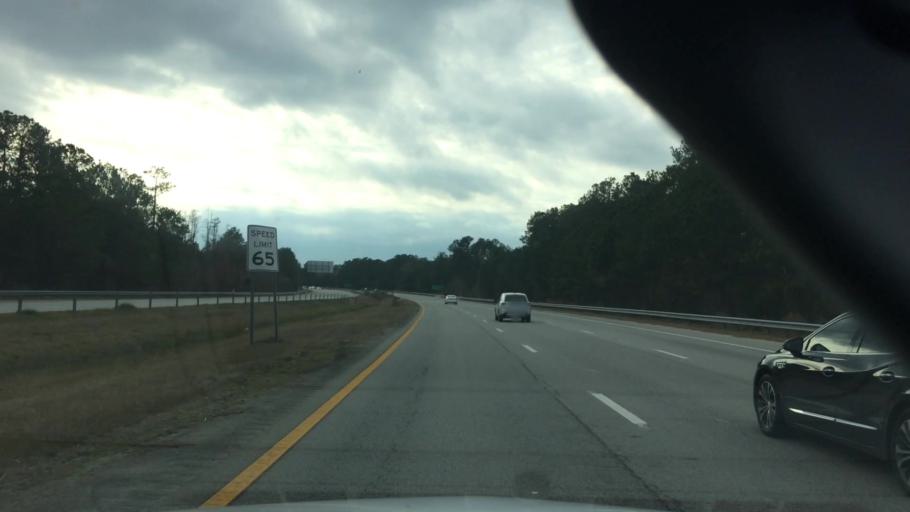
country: US
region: South Carolina
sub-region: Horry County
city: North Myrtle Beach
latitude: 33.8703
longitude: -78.6895
